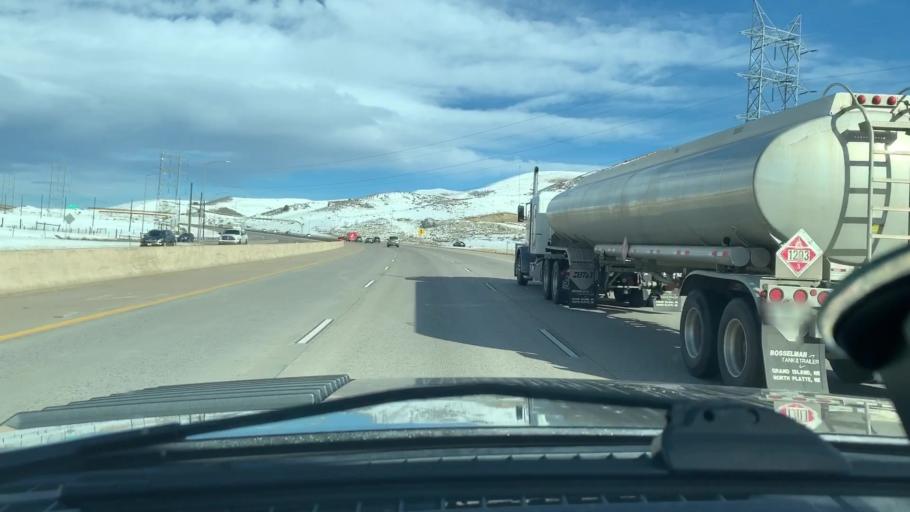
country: US
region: Colorado
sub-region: Jefferson County
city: West Pleasant View
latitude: 39.6882
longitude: -105.1876
